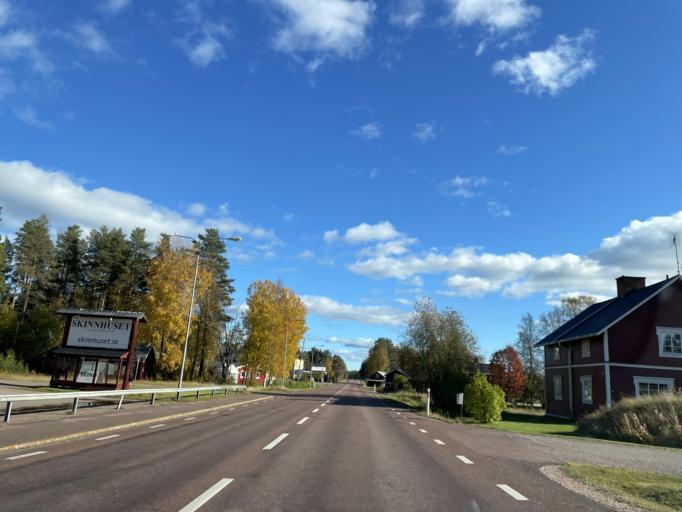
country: SE
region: Dalarna
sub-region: Malung-Saelens kommun
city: Malung
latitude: 60.7341
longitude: 13.5585
